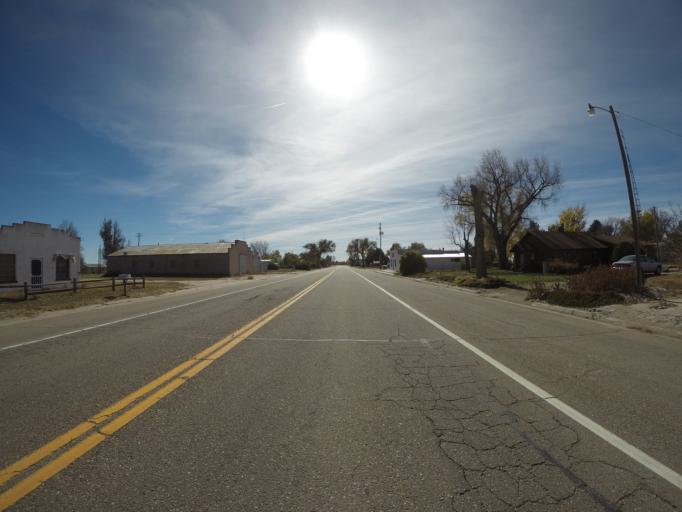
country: US
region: Colorado
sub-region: Yuma County
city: Yuma
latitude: 39.6655
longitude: -102.8509
